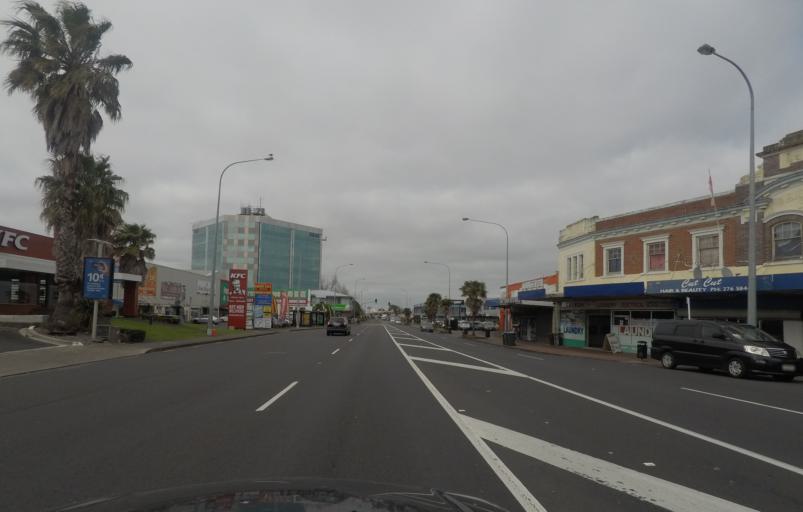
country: NZ
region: Auckland
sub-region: Auckland
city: Mangere
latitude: -36.9456
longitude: 174.8452
